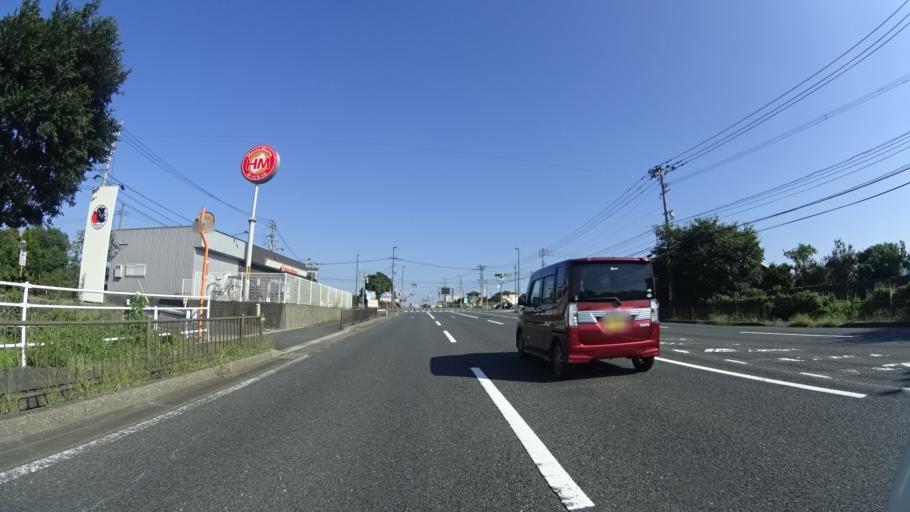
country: JP
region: Fukuoka
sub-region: Buzen-shi
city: Buzen
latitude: 33.6062
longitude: 131.1169
